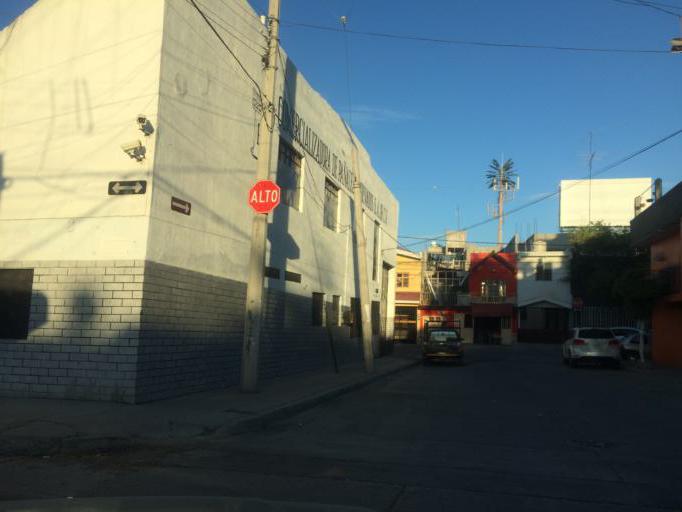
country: MX
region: Guanajuato
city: Leon
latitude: 21.1345
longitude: -101.6985
